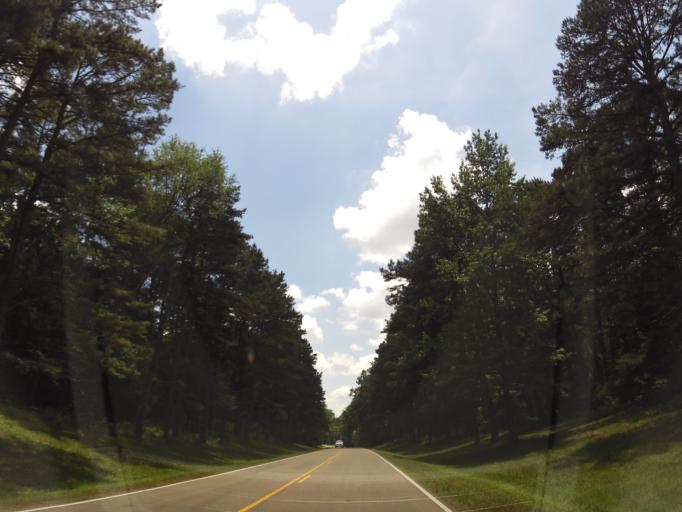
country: US
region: Mississippi
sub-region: Lee County
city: Saltillo
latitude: 34.3251
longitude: -88.7141
